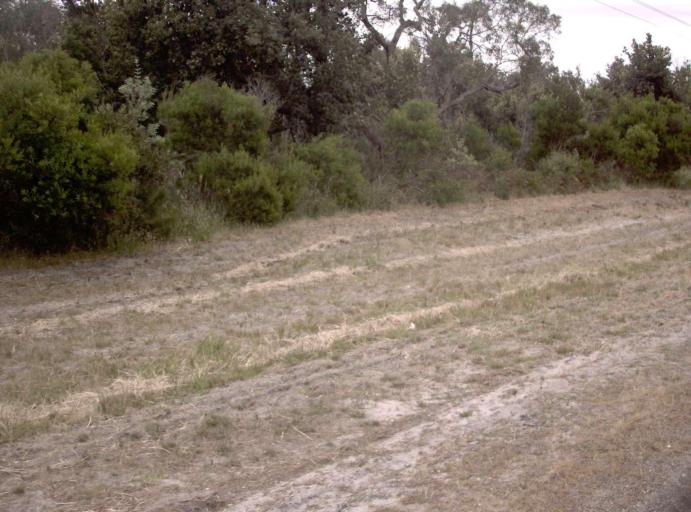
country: AU
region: Victoria
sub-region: East Gippsland
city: Bairnsdale
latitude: -38.0632
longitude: 147.5600
